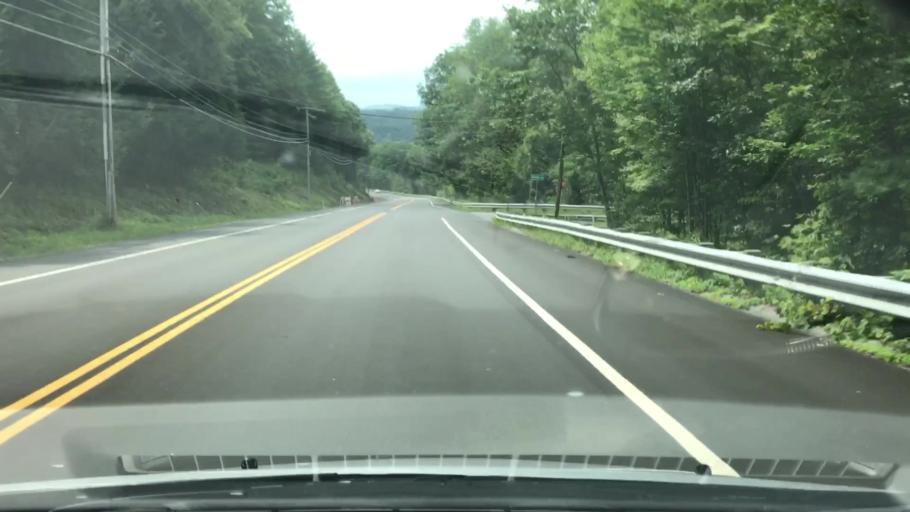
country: US
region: New Hampshire
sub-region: Grafton County
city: Hanover
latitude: 43.7488
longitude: -72.2247
